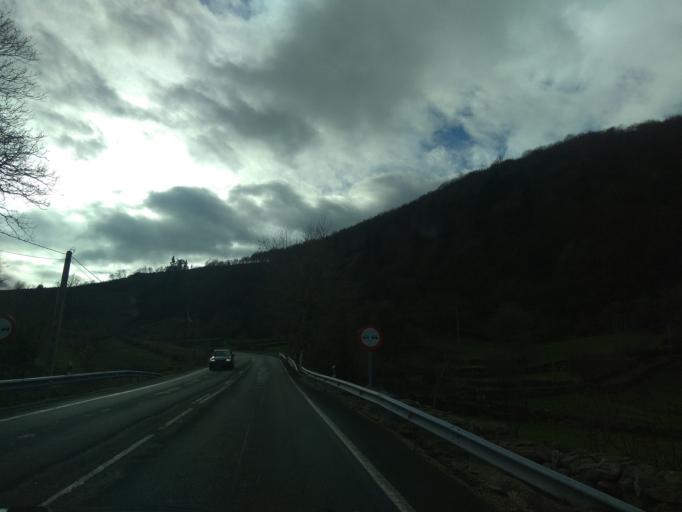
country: ES
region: Cantabria
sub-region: Provincia de Cantabria
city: San Pedro del Romeral
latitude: 43.0811
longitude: -3.8937
